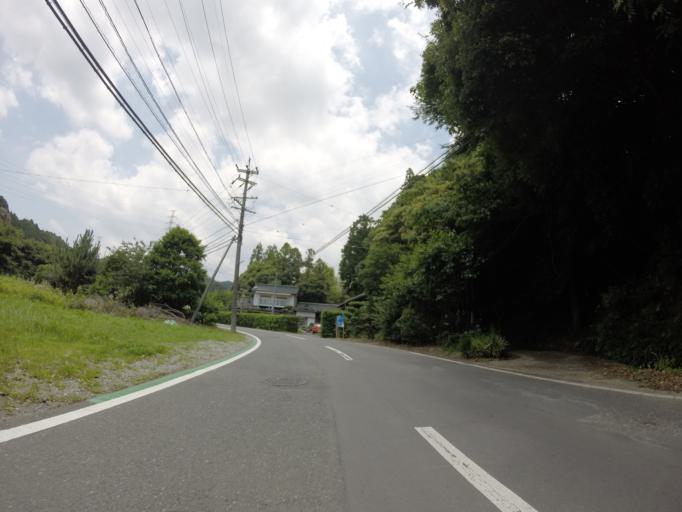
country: JP
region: Shizuoka
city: Kanaya
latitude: 34.8117
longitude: 138.0690
